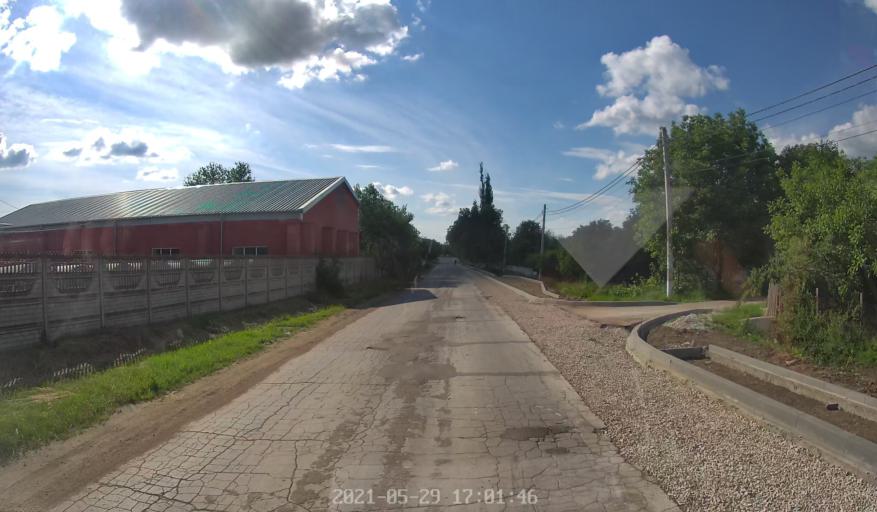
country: MD
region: Laloveni
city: Ialoveni
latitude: 46.8330
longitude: 28.8563
